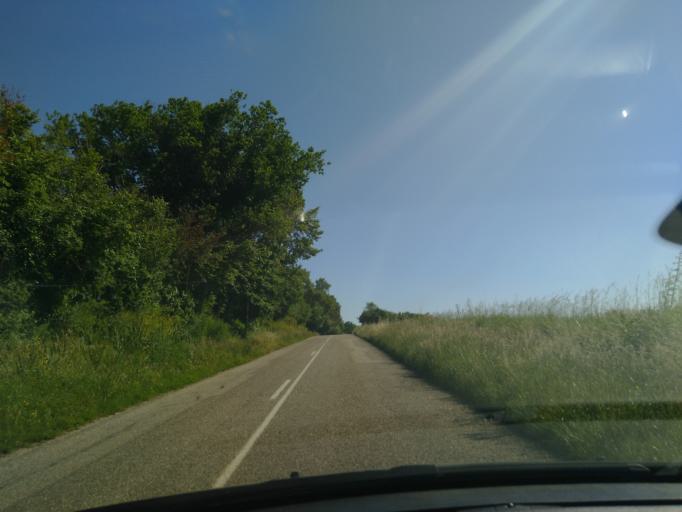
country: FR
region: Midi-Pyrenees
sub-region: Departement du Gers
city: Gimont
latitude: 43.5832
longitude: 0.8225
